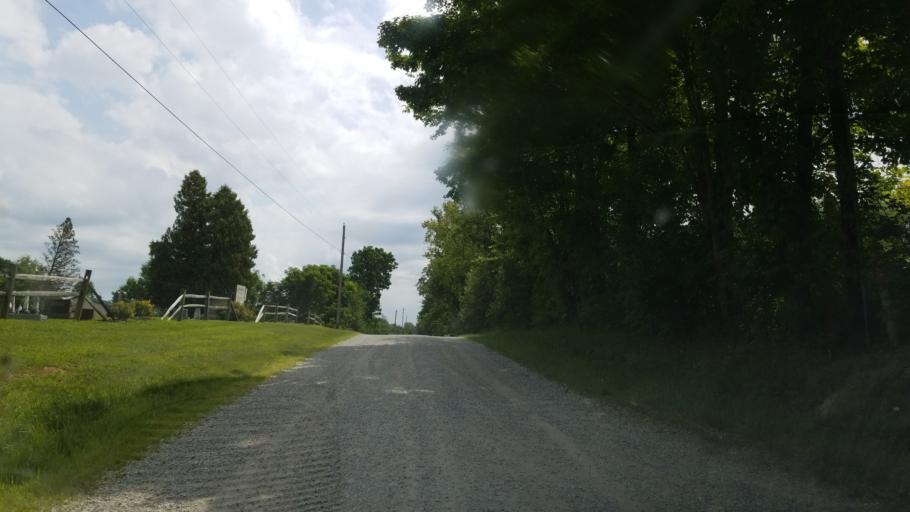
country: US
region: Ohio
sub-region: Delaware County
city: Sunbury
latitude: 40.3257
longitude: -82.8113
